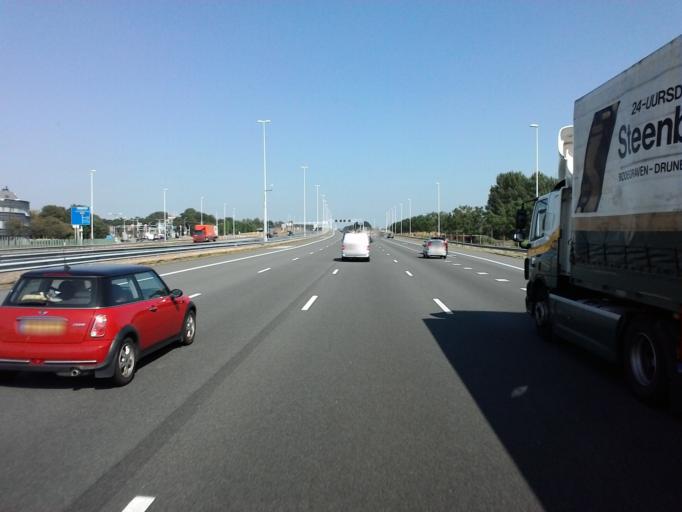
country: NL
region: Utrecht
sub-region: Gemeente Bunnik
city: Bunnik
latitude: 52.0600
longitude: 5.2079
